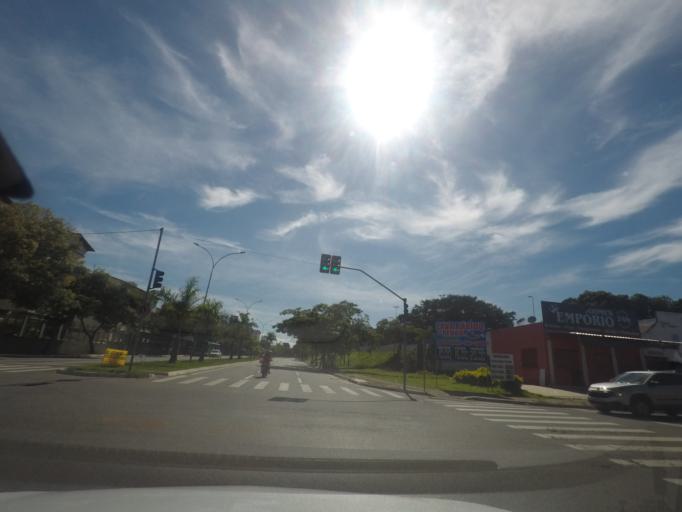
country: BR
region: Goias
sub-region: Goiania
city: Goiania
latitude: -16.6648
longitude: -49.2668
